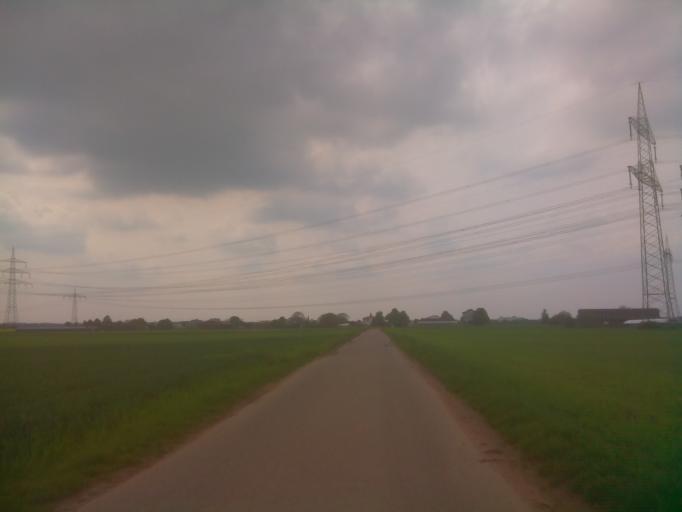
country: DE
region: Baden-Wuerttemberg
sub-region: Karlsruhe Region
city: Plankstadt
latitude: 49.3824
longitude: 8.6103
